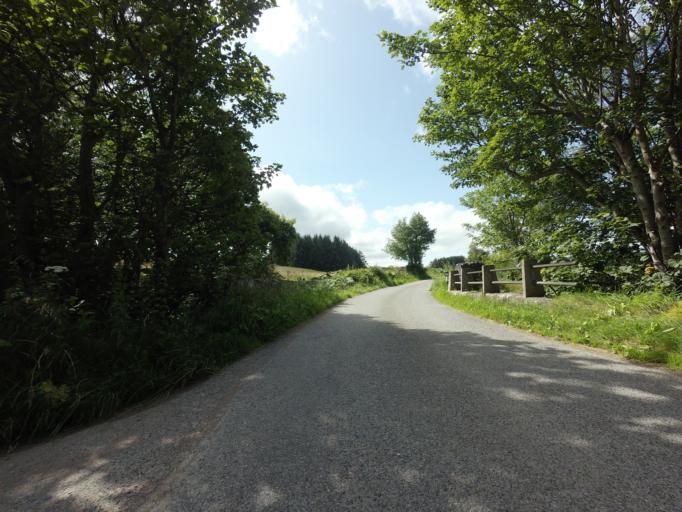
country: GB
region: Scotland
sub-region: Highland
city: Nairn
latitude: 57.4968
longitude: -3.9993
